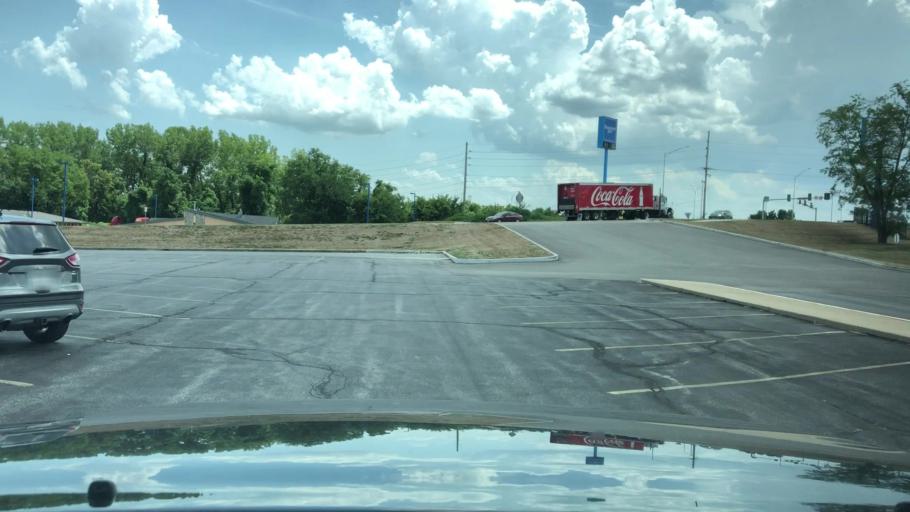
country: US
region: Missouri
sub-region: Saint Charles County
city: Saint Peters
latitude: 38.7965
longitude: -90.5641
